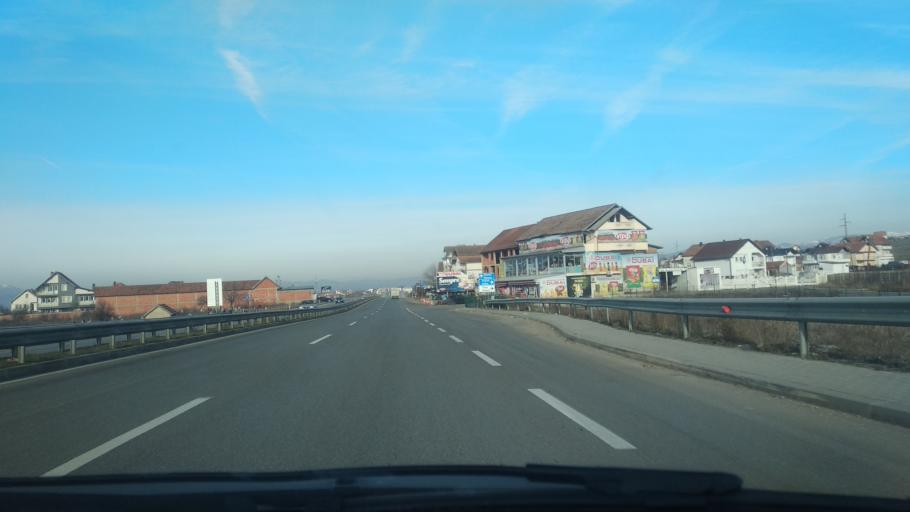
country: XK
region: Pristina
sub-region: Komuna e Obiliqit
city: Obiliq
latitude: 42.7526
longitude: 21.0393
